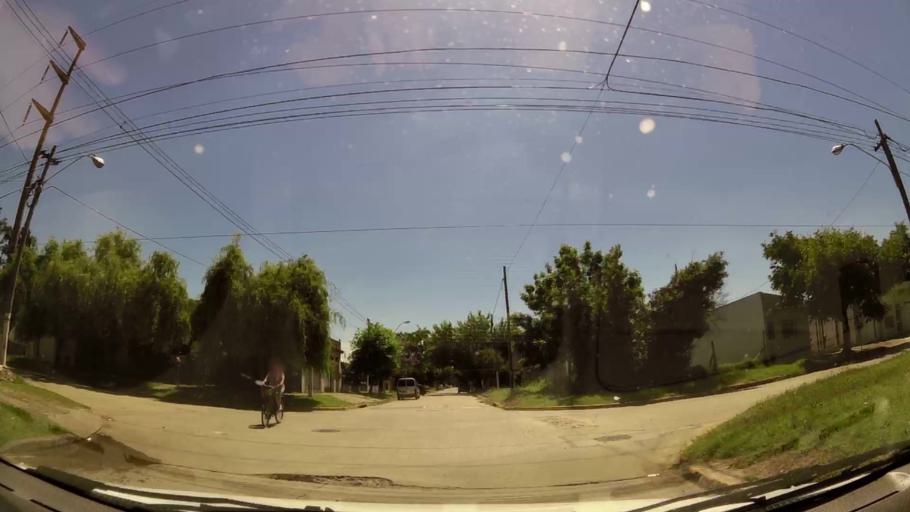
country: AR
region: Buenos Aires
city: Ituzaingo
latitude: -34.6782
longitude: -58.6749
